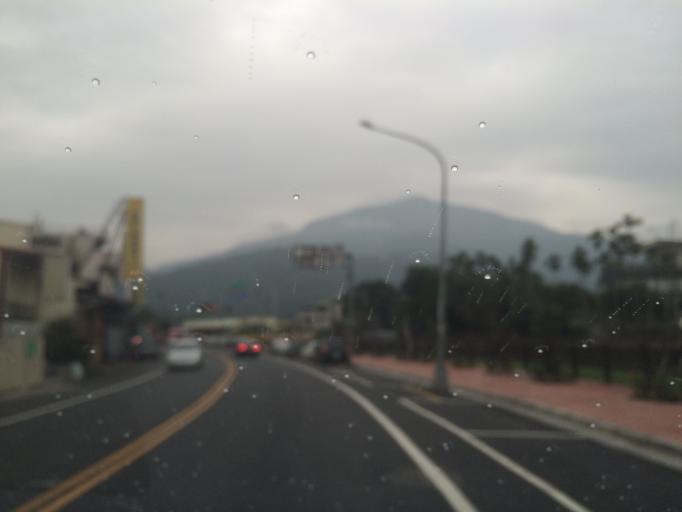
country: TW
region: Taiwan
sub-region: Nantou
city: Puli
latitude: 23.9562
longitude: 120.9719
